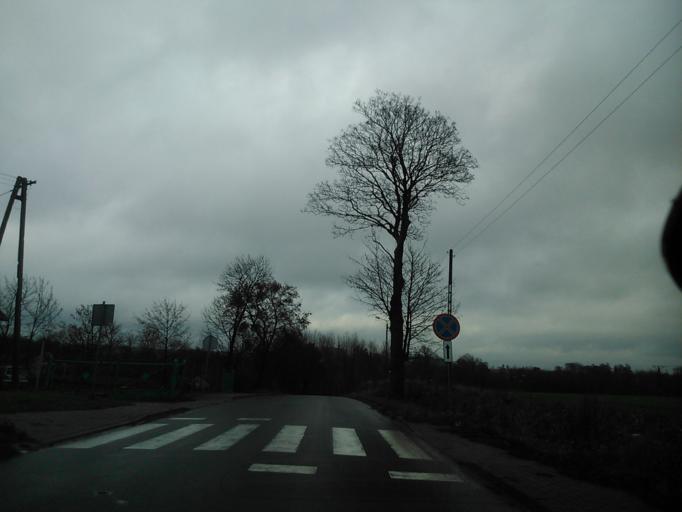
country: PL
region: Kujawsko-Pomorskie
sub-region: Powiat golubsko-dobrzynski
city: Radomin
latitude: 53.1221
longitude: 19.1678
